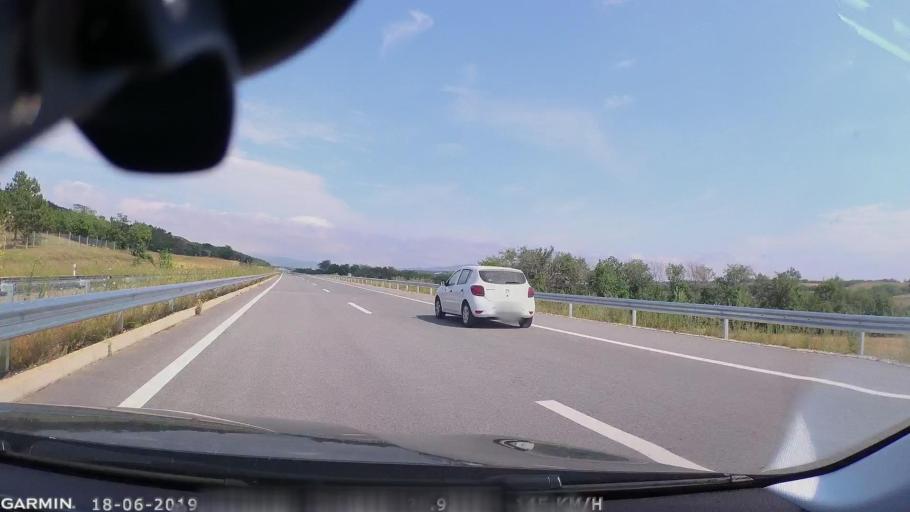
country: MK
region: Sveti Nikole
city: Sveti Nikole
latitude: 41.8932
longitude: 21.9256
